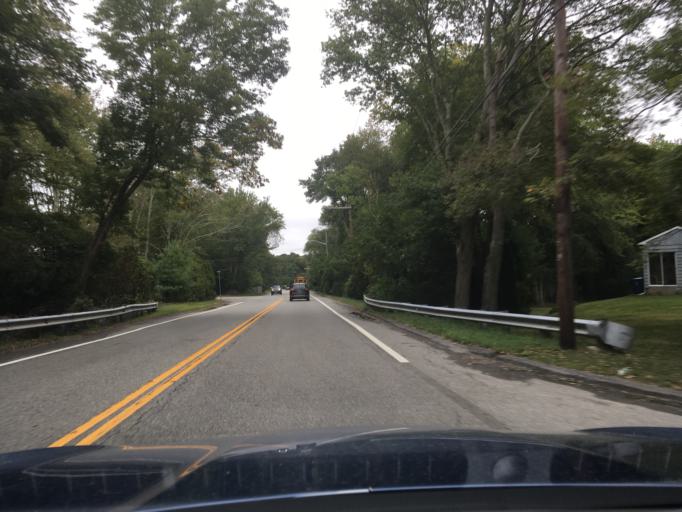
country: US
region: Rhode Island
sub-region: Kent County
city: East Greenwich
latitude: 41.6612
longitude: -71.4629
